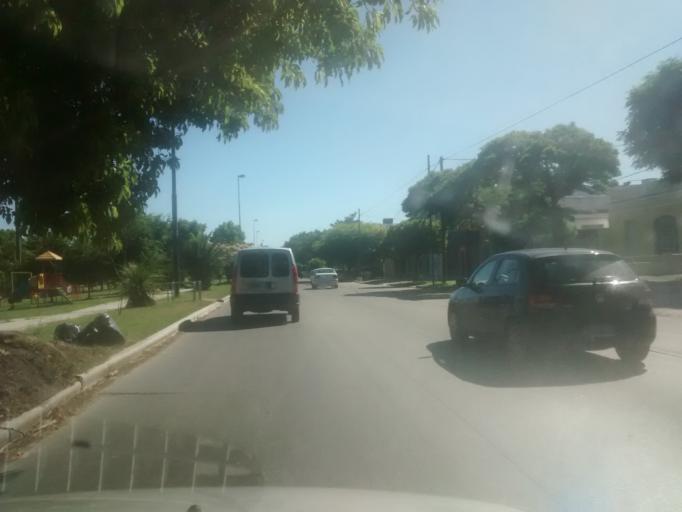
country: AR
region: Buenos Aires
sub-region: Partido de La Plata
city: La Plata
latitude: -34.9272
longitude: -57.9237
